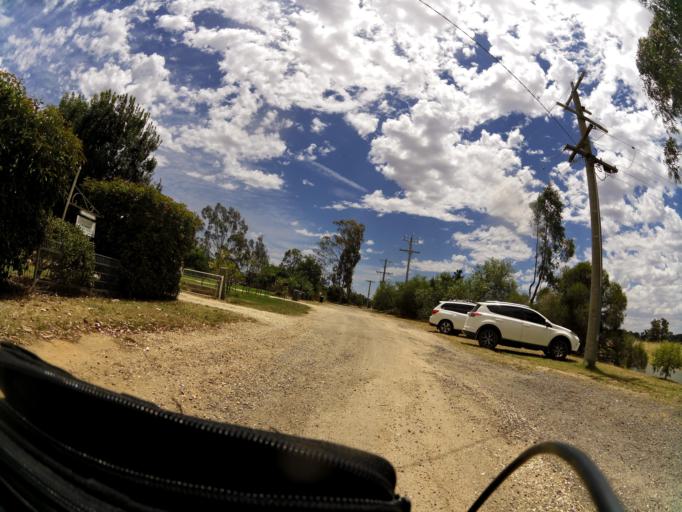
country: AU
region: Victoria
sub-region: Campaspe
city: Kyabram
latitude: -36.7442
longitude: 145.1379
